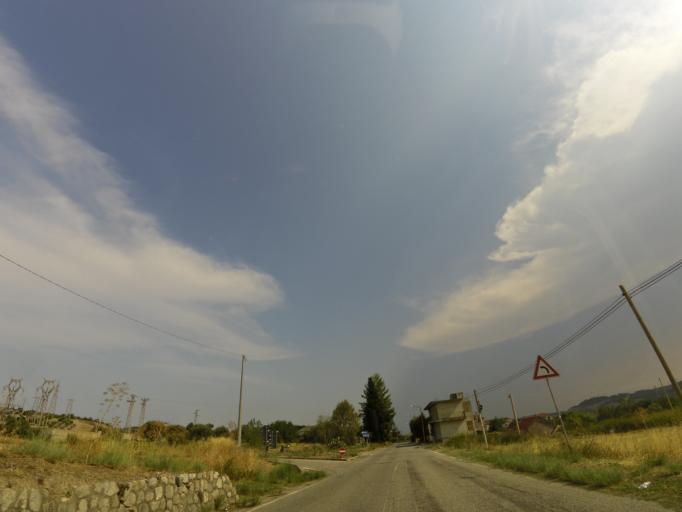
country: IT
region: Calabria
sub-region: Provincia di Reggio Calabria
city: Monasterace
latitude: 38.4475
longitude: 16.5340
